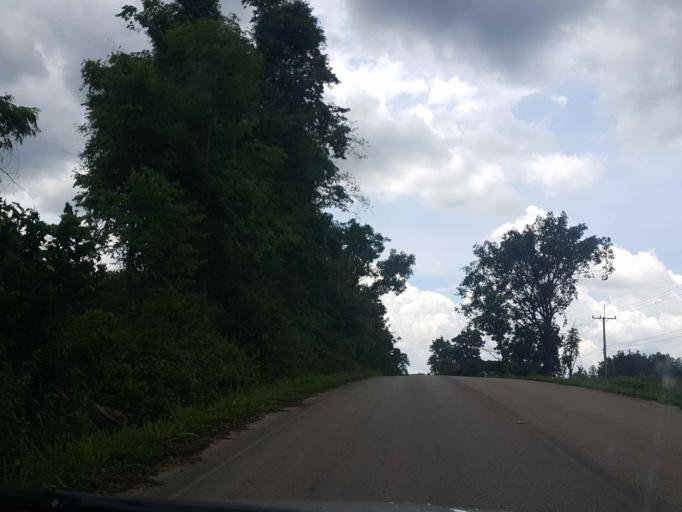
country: TH
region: Lampang
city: Ngao
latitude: 18.9561
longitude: 100.0745
